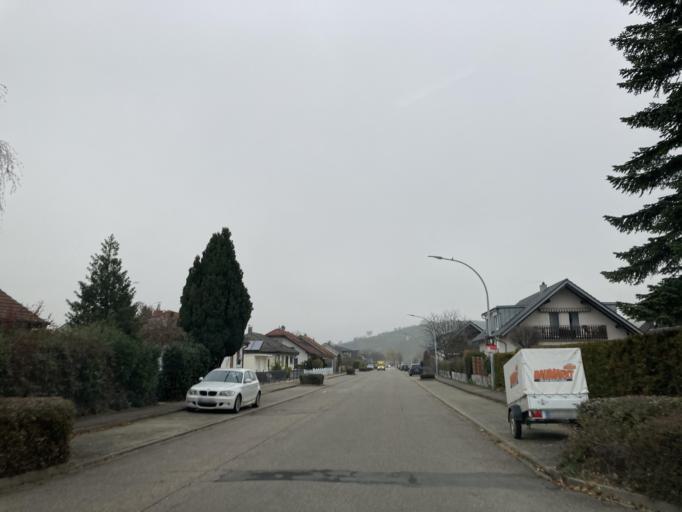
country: DE
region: Baden-Wuerttemberg
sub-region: Freiburg Region
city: Auggen
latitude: 47.7916
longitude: 7.5954
